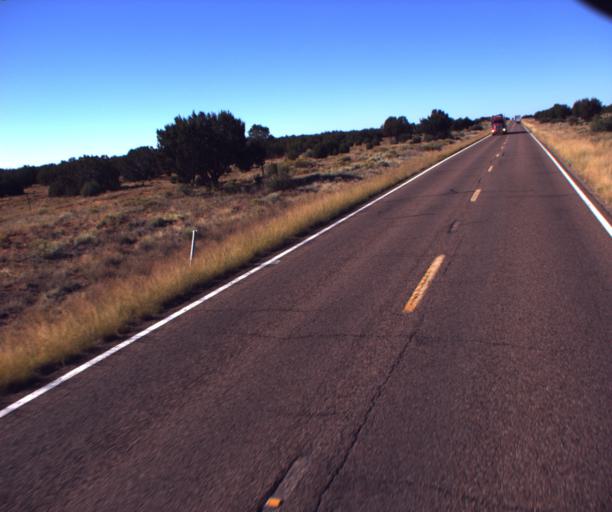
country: US
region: Arizona
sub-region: Navajo County
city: Heber-Overgaard
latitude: 34.5230
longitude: -110.4307
